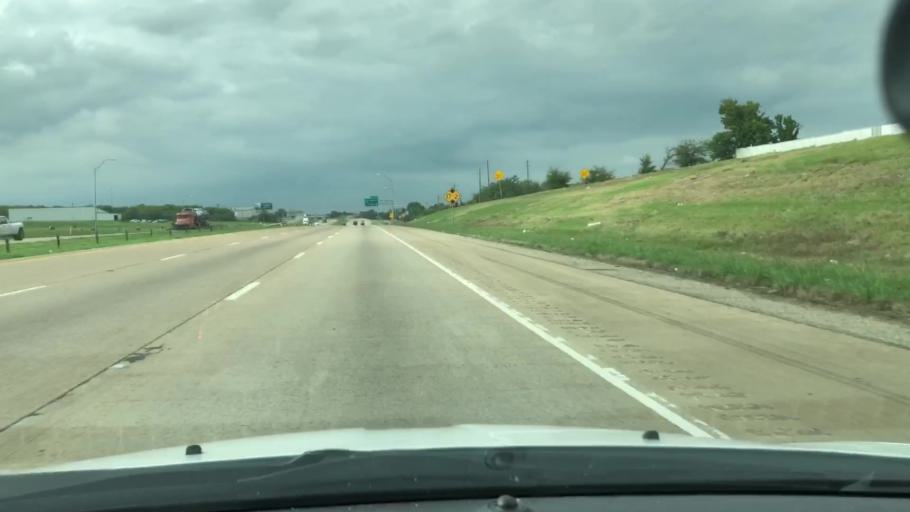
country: US
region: Texas
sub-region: Ellis County
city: Ennis
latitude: 32.3491
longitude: -96.6247
